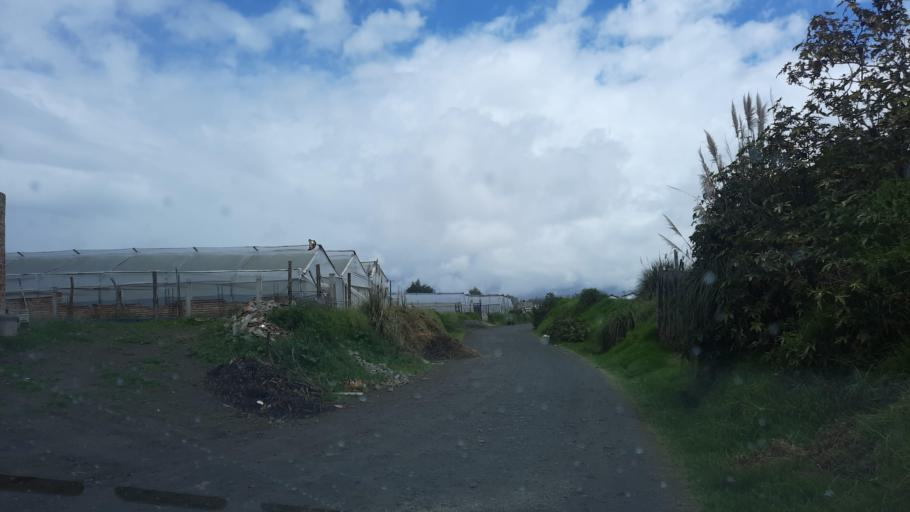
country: EC
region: Chimborazo
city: Riobamba
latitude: -1.6905
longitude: -78.6695
